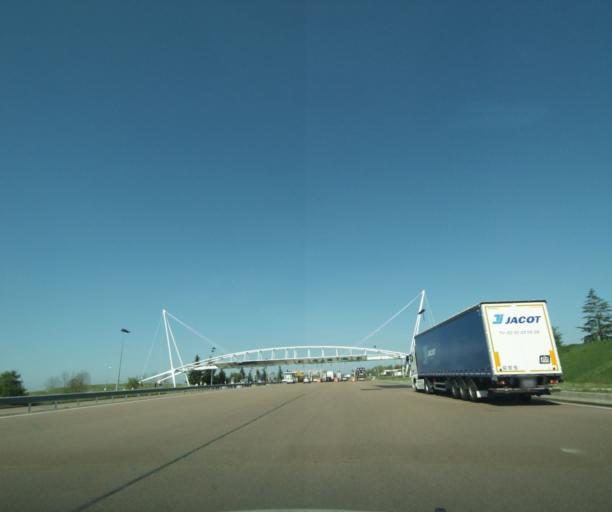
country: FR
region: Bourgogne
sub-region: Departement de la Nievre
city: Cosne-Cours-sur-Loire
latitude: 47.4362
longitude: 2.9401
